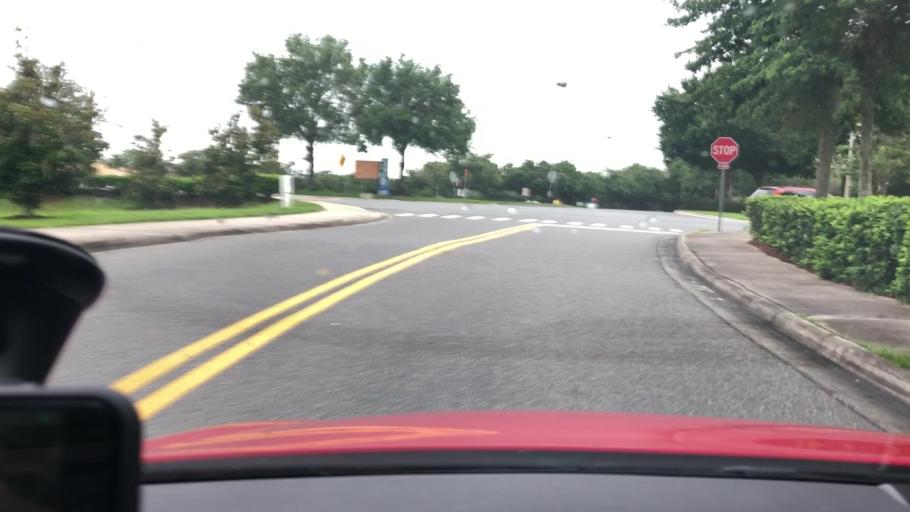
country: US
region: Florida
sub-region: Lake County
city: Mount Dora
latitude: 28.8195
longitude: -81.6704
